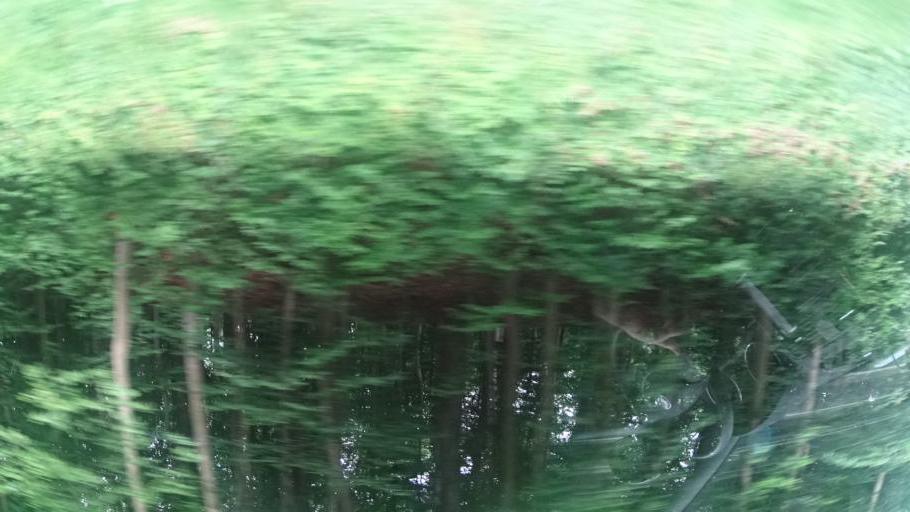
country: DE
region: Lower Saxony
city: Wennigsen
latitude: 52.2250
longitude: 9.6302
